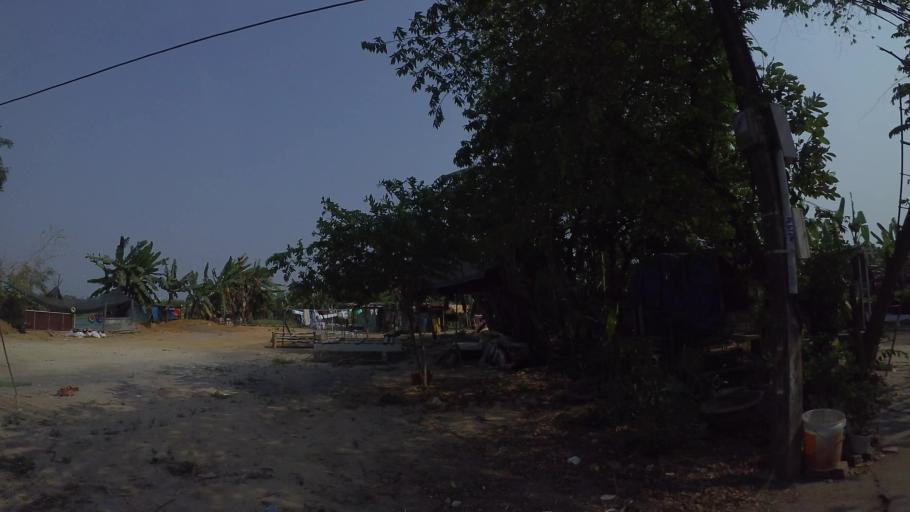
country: VN
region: Da Nang
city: Cam Le
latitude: 16.0024
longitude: 108.1936
